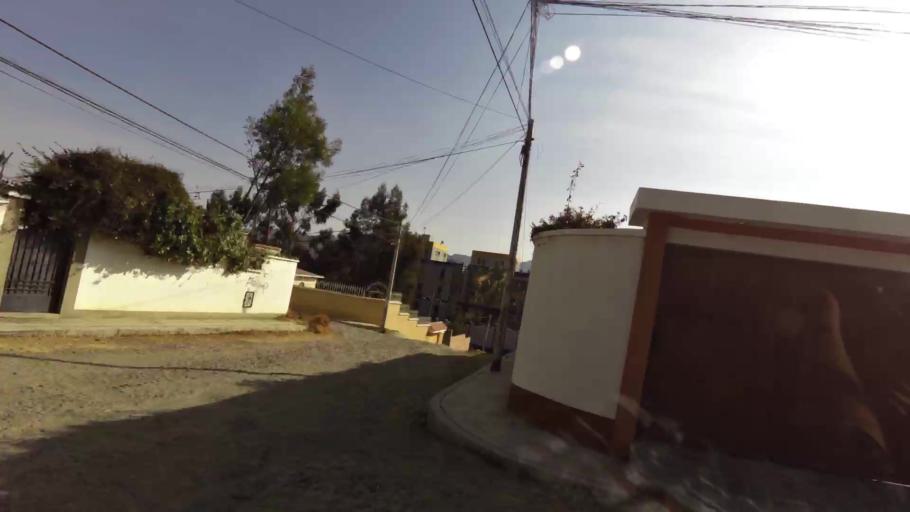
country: BO
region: La Paz
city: La Paz
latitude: -16.5300
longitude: -68.0809
